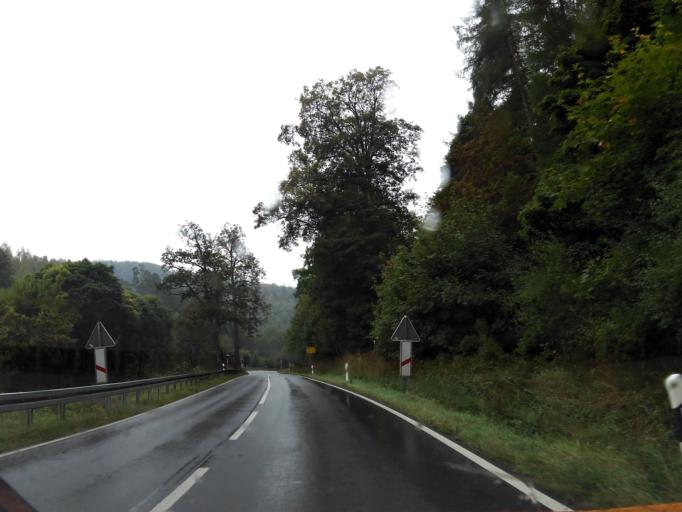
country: DE
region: Saxony-Anhalt
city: Harzgerode
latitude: 51.6717
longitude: 11.1340
